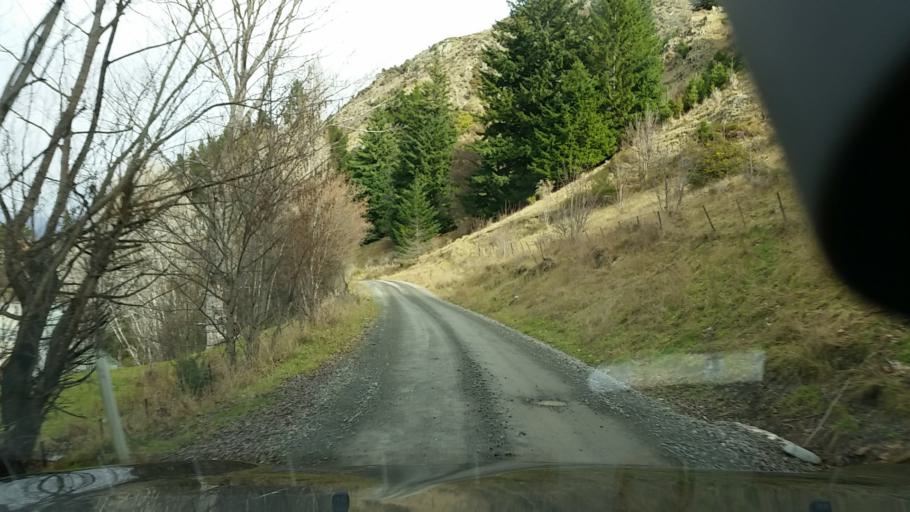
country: NZ
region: Tasman
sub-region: Tasman District
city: Richmond
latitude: -41.7209
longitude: 173.4707
